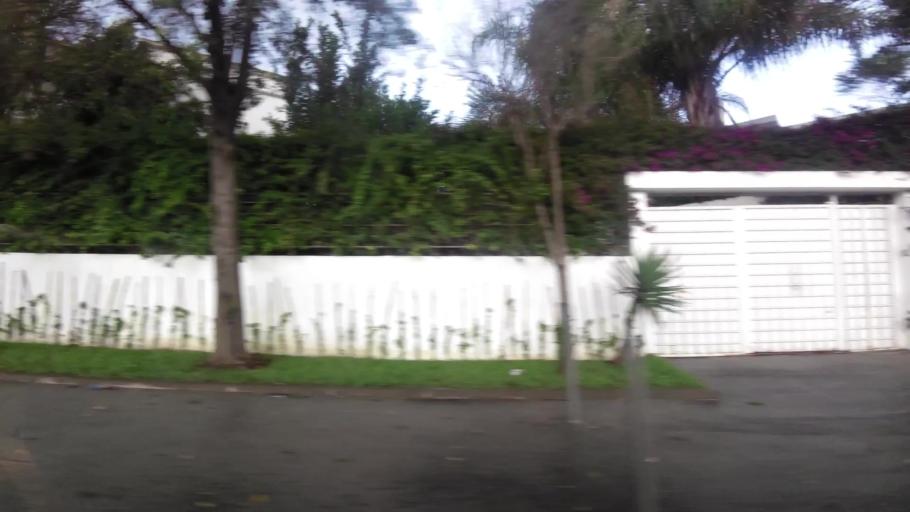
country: MA
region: Grand Casablanca
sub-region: Casablanca
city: Casablanca
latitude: 33.5392
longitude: -7.6673
